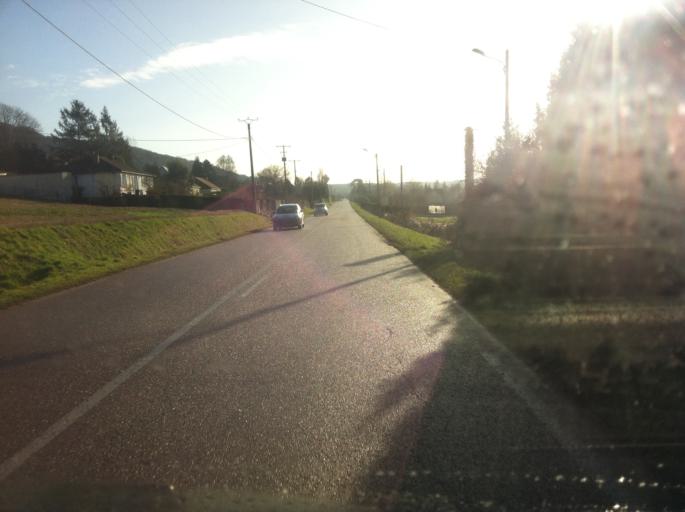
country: FR
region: Haute-Normandie
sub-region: Departement de la Seine-Maritime
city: Henouville
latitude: 49.4749
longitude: 0.9452
